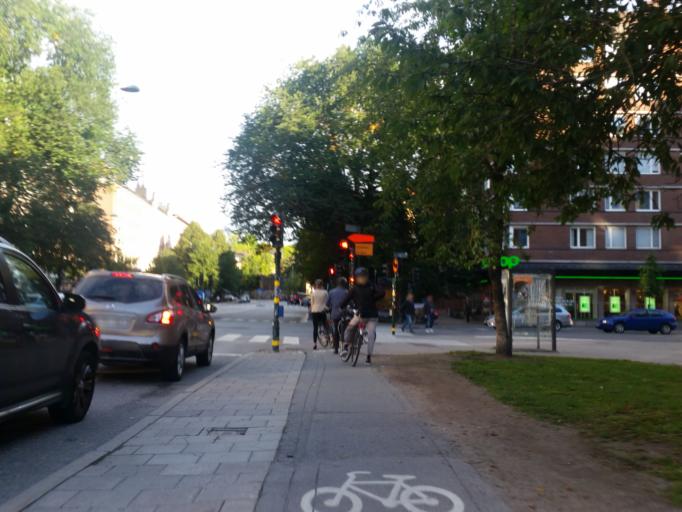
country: SE
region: Stockholm
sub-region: Stockholms Kommun
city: Arsta
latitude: 59.3172
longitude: 18.0510
